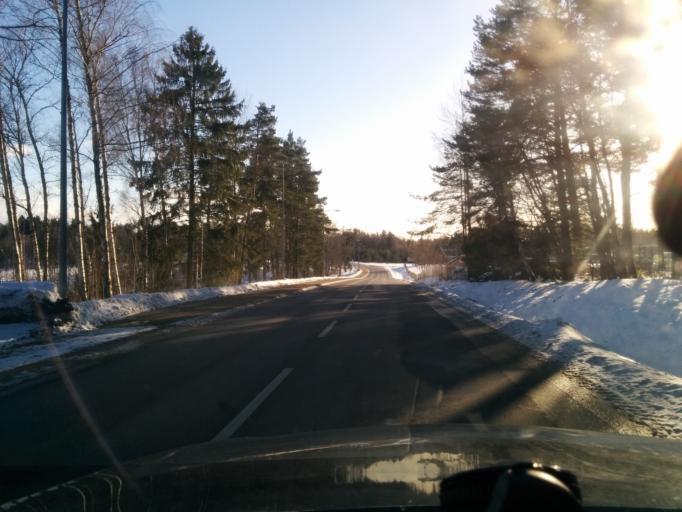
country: SE
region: Stockholm
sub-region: Taby Kommun
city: Taby
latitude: 59.4795
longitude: 18.0940
